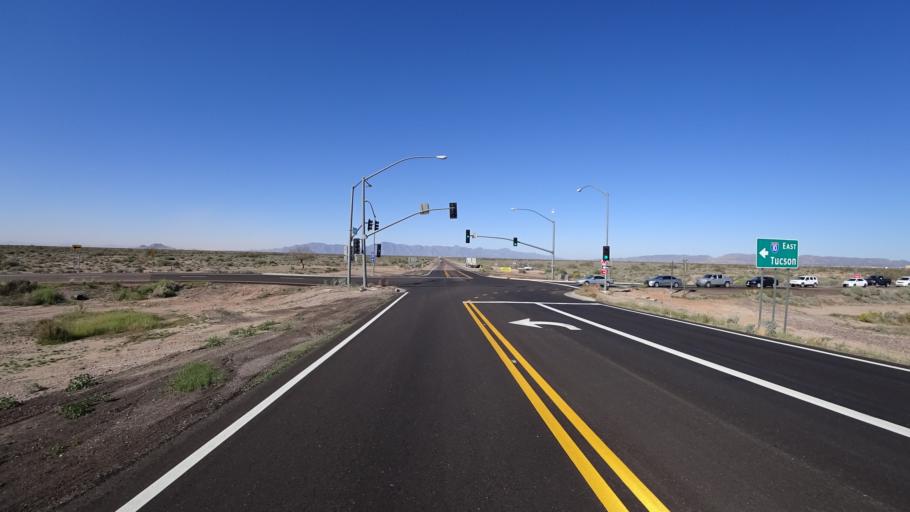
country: US
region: Arizona
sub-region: Maricopa County
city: Sun Lakes
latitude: 33.2192
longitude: -111.9225
